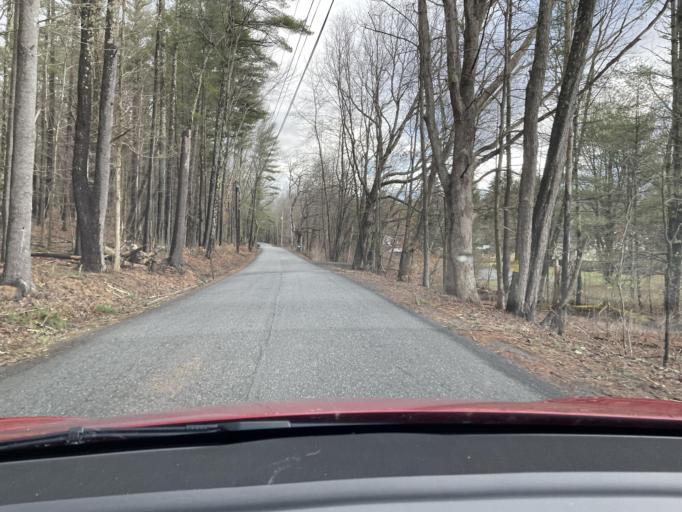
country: US
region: New York
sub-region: Ulster County
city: Zena
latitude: 42.0700
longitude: -74.0448
